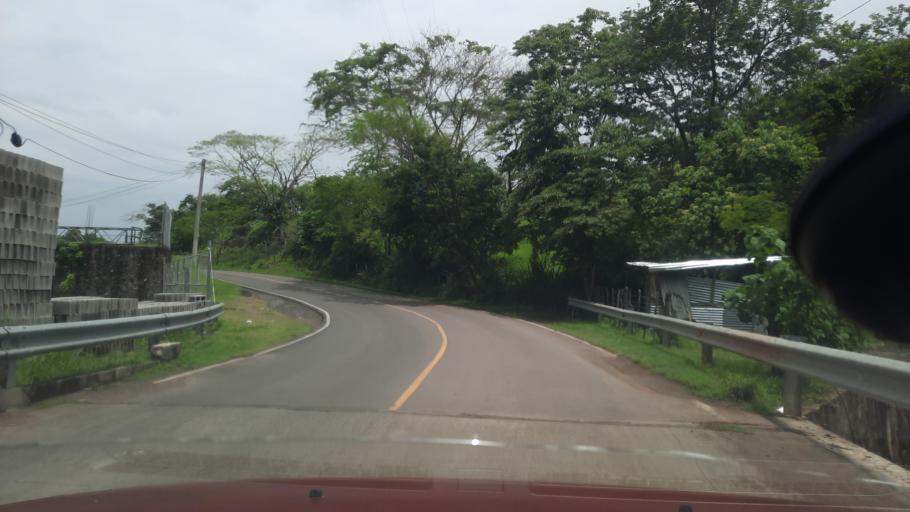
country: SV
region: La Union
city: Santa Rosa de Lima
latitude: 13.6497
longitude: -87.8461
